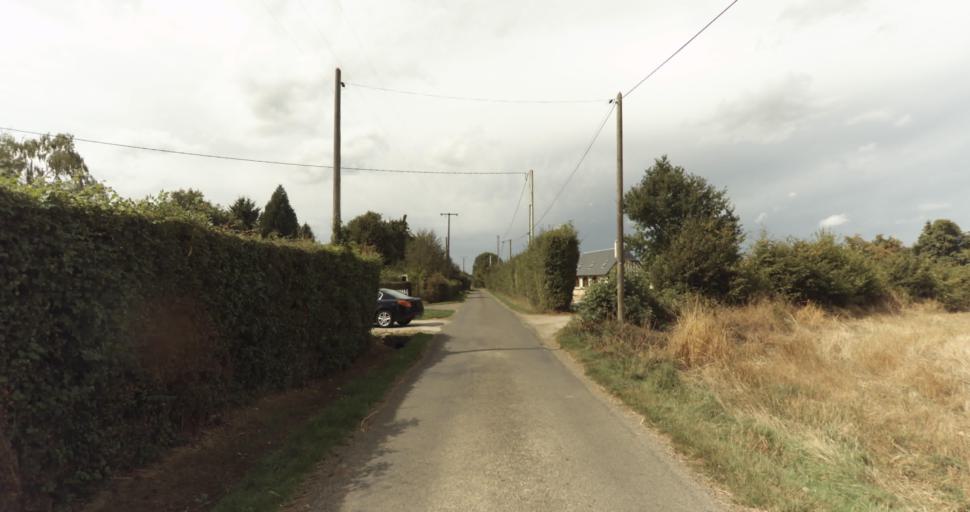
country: FR
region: Lower Normandy
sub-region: Departement du Calvados
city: Orbec
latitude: 48.9250
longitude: 0.3761
